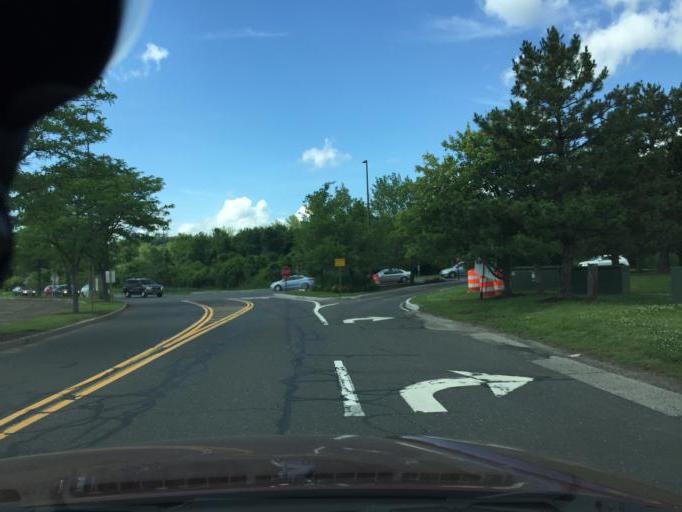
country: US
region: Connecticut
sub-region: Fairfield County
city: Danbury
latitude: 41.3816
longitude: -73.4763
